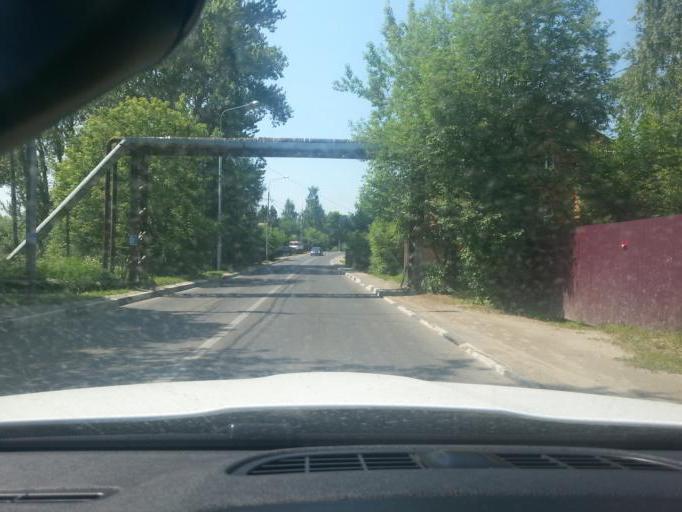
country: RU
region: Moskovskaya
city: Zheleznodorozhnyy
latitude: 55.7264
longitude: 38.0167
